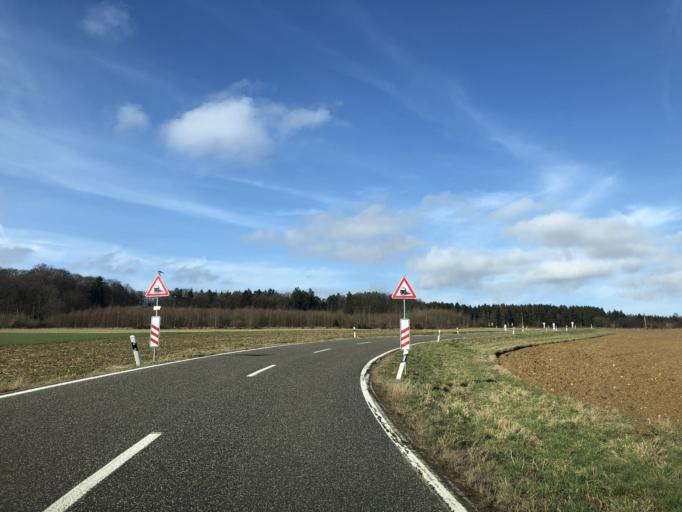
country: DE
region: Rheinland-Pfalz
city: Wahlenau
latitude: 49.9089
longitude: 7.2453
